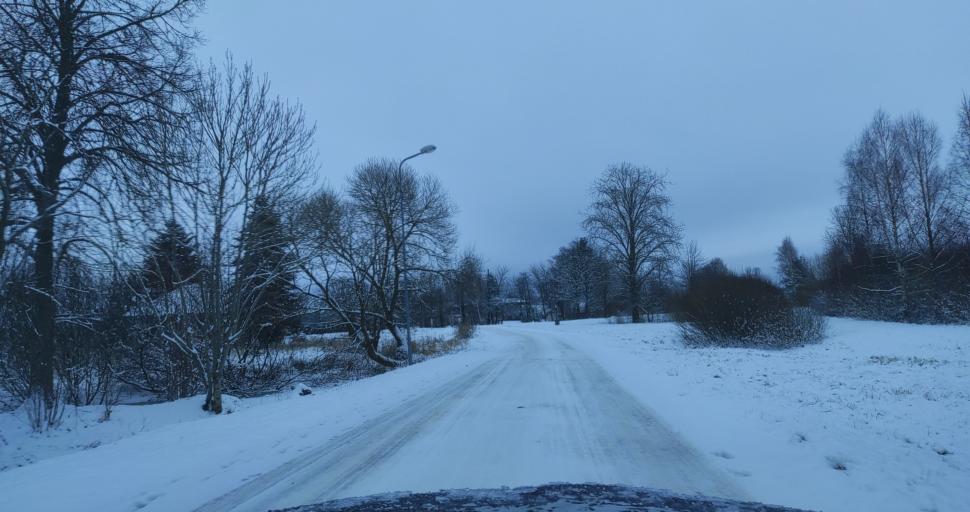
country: LV
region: Alsunga
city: Alsunga
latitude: 56.9773
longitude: 21.5596
